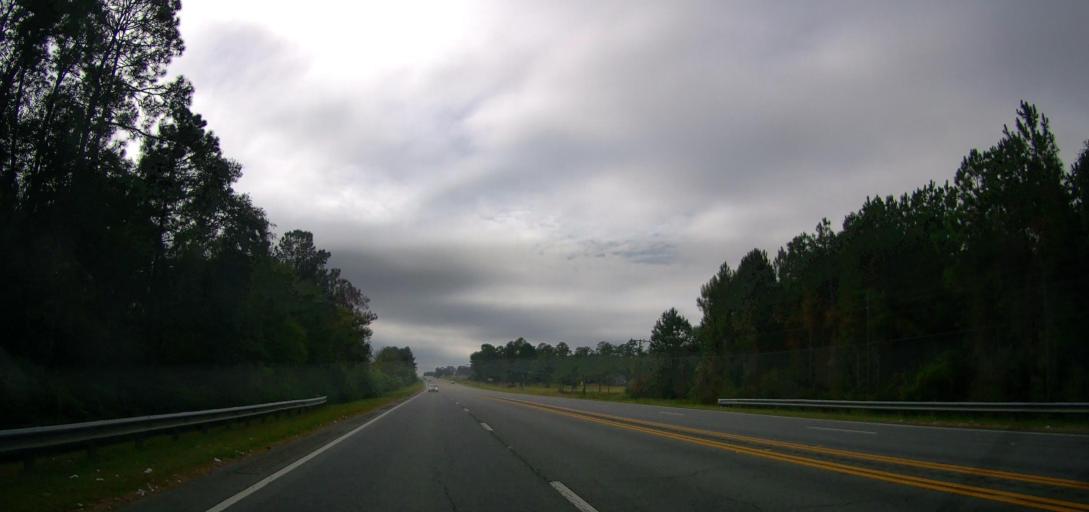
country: US
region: Georgia
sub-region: Tift County
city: Omega
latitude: 31.3821
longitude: -83.5550
